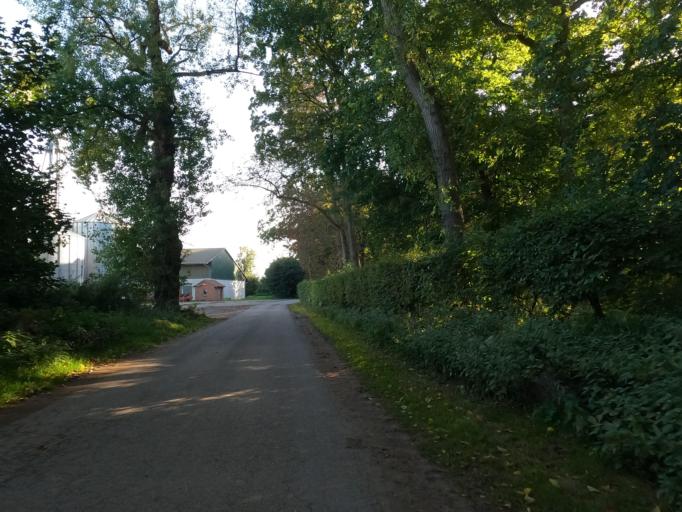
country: DE
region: Schleswig-Holstein
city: Neukirchen
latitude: 54.3156
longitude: 11.0229
